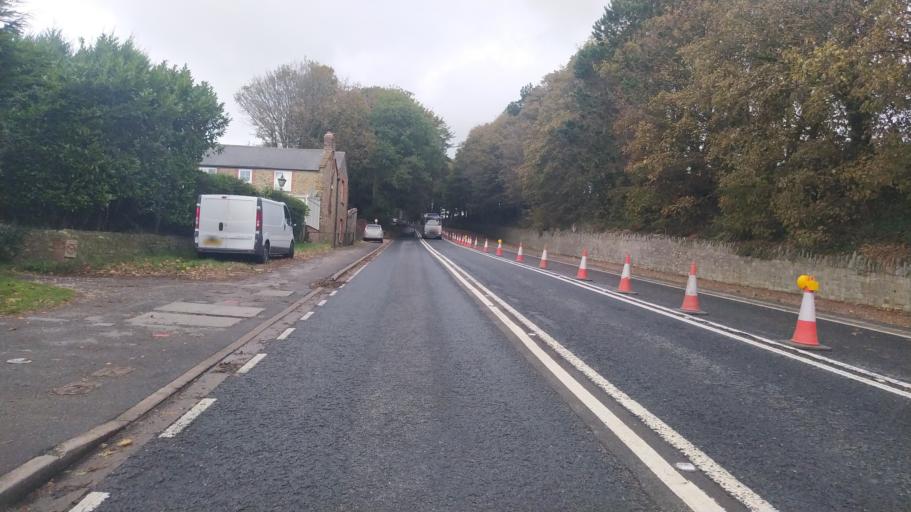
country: GB
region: England
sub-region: Dorset
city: Bridport
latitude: 50.7345
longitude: -2.8278
